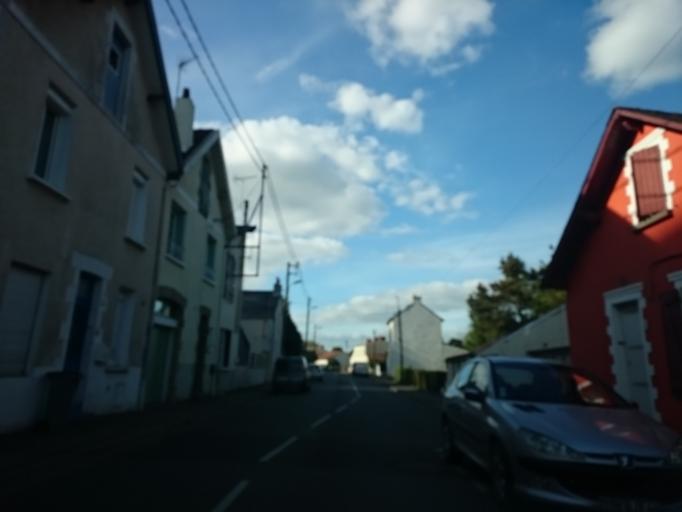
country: FR
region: Pays de la Loire
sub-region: Departement de la Loire-Atlantique
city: Indre
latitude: 47.1974
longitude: -1.6670
